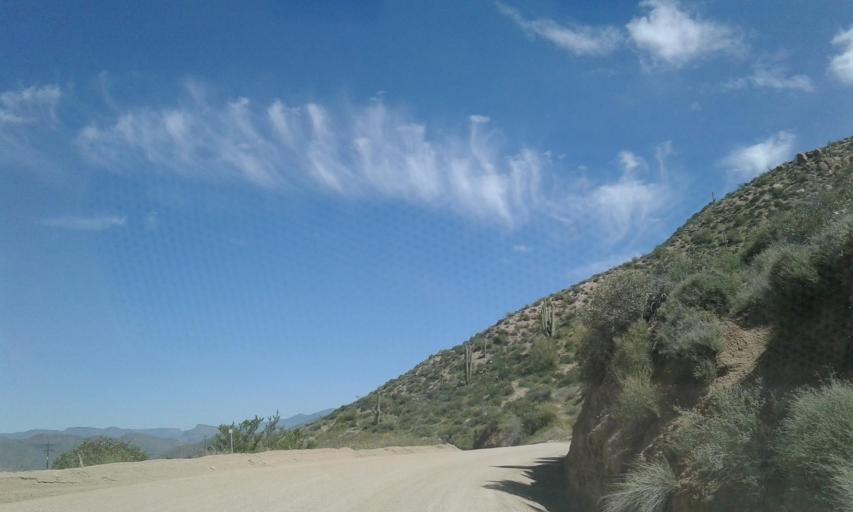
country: US
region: Arizona
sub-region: Gila County
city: Tonto Basin
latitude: 33.5733
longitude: -111.2309
